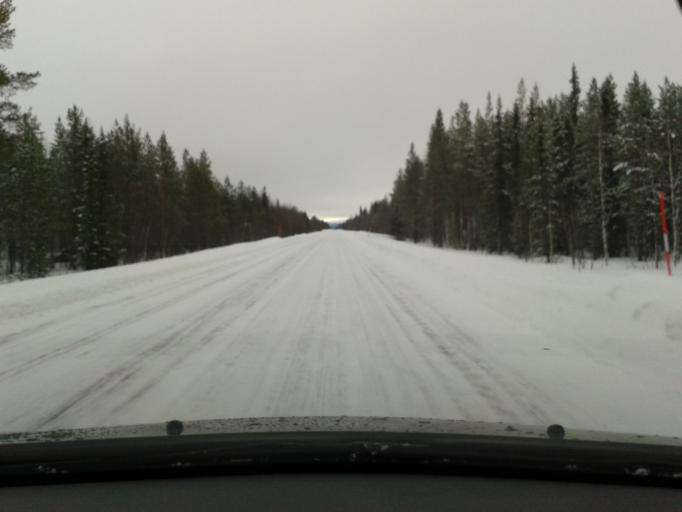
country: SE
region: Vaesterbotten
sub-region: Vilhelmina Kommun
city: Sjoberg
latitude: 64.8519
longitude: 15.9057
